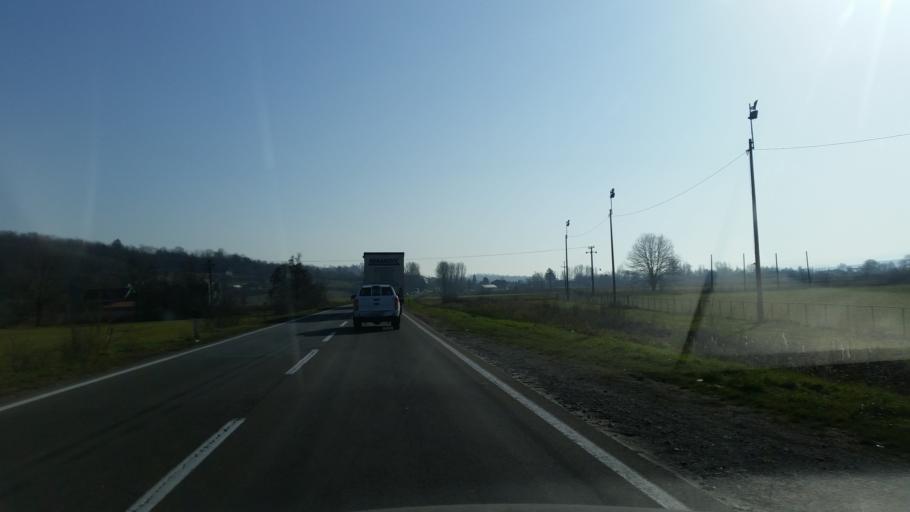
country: RS
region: Central Serbia
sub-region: Kolubarski Okrug
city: Lajkovac
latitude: 44.3418
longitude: 20.2049
